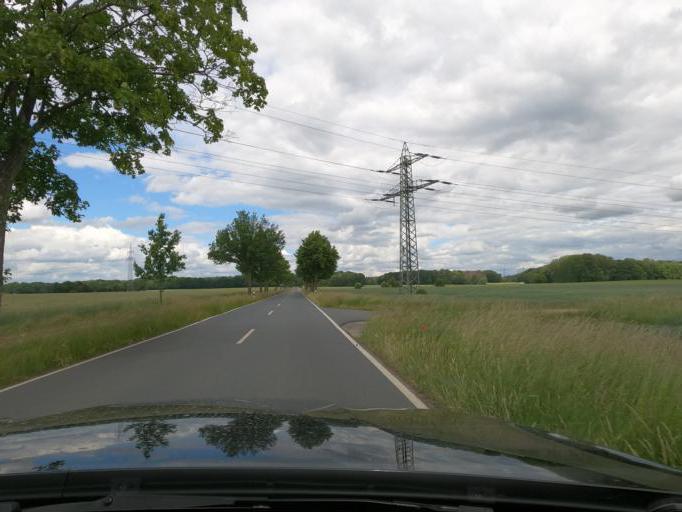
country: DE
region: Lower Saxony
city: Lehrte
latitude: 52.3812
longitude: 9.9241
